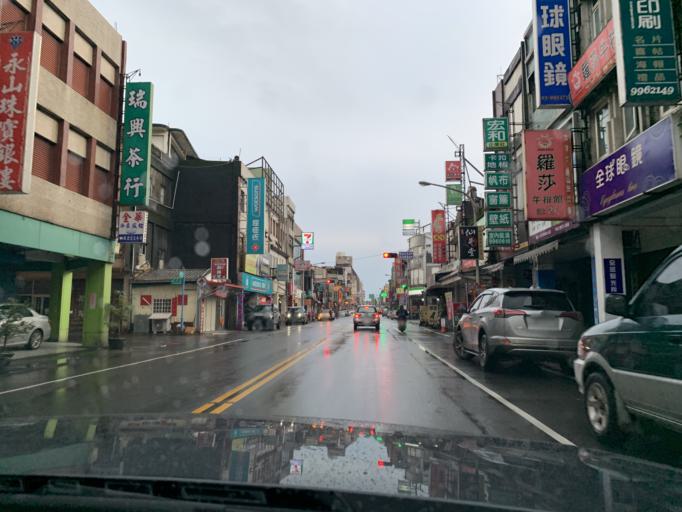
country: TW
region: Taiwan
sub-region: Yilan
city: Yilan
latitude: 24.5960
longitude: 121.8508
